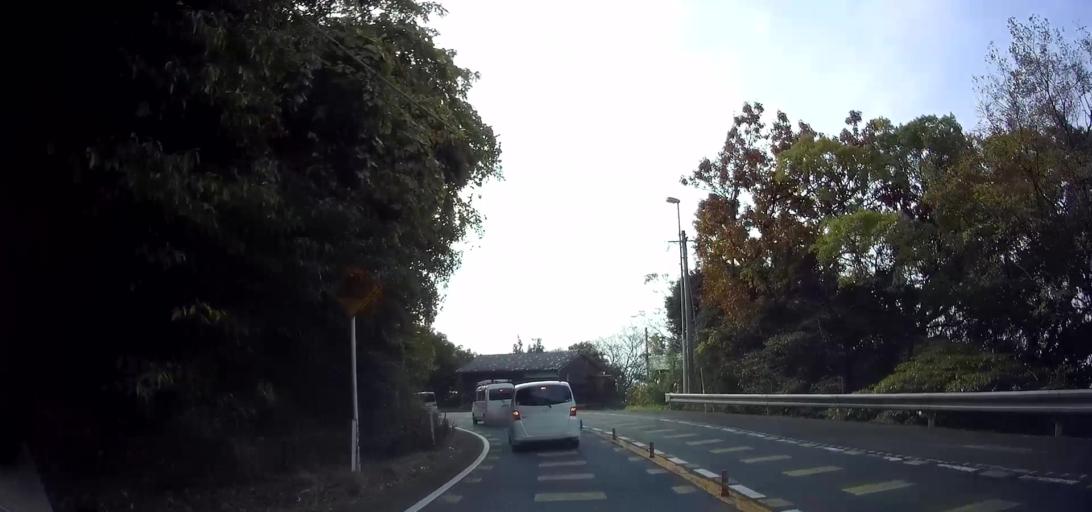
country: JP
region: Nagasaki
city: Shimabara
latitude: 32.7580
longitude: 130.2031
